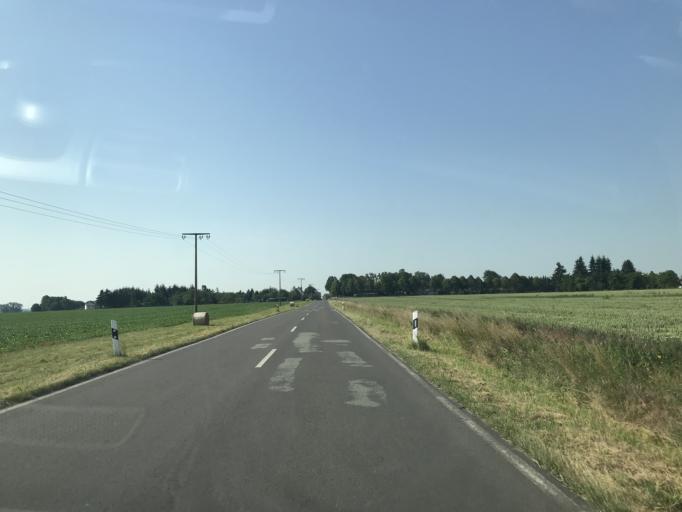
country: DE
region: Saxony-Anhalt
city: Altenhausen
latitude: 52.2609
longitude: 11.2250
